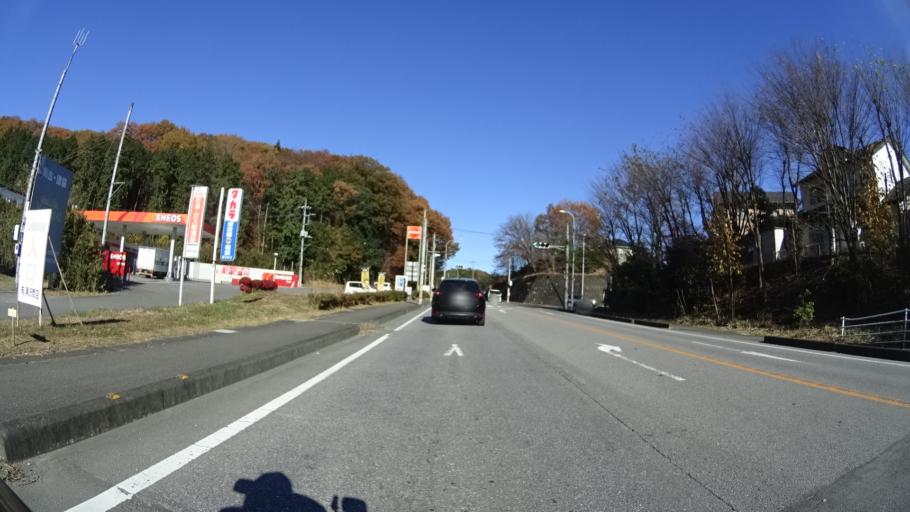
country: JP
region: Tochigi
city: Utsunomiya-shi
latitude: 36.5988
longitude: 139.8128
